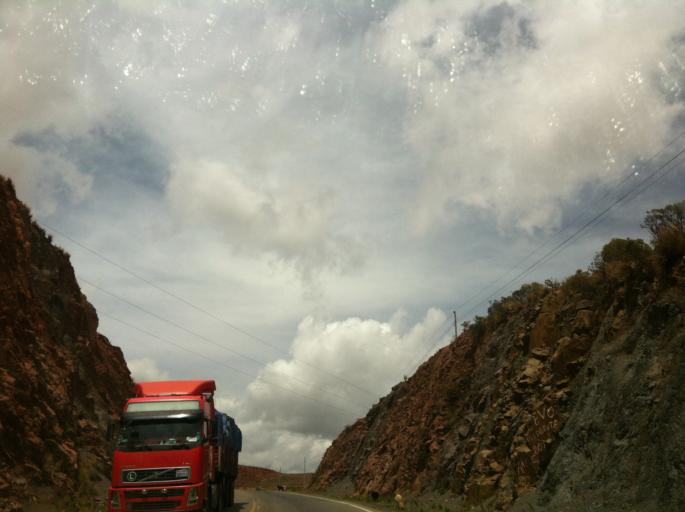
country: BO
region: Cochabamba
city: Colchani
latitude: -17.7065
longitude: -66.6819
